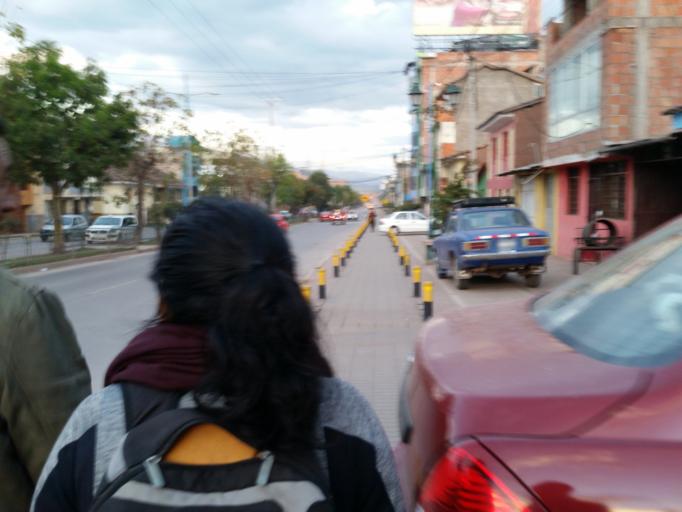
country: PE
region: Cusco
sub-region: Provincia de Cusco
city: Cusco
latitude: -13.5369
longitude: -71.9539
